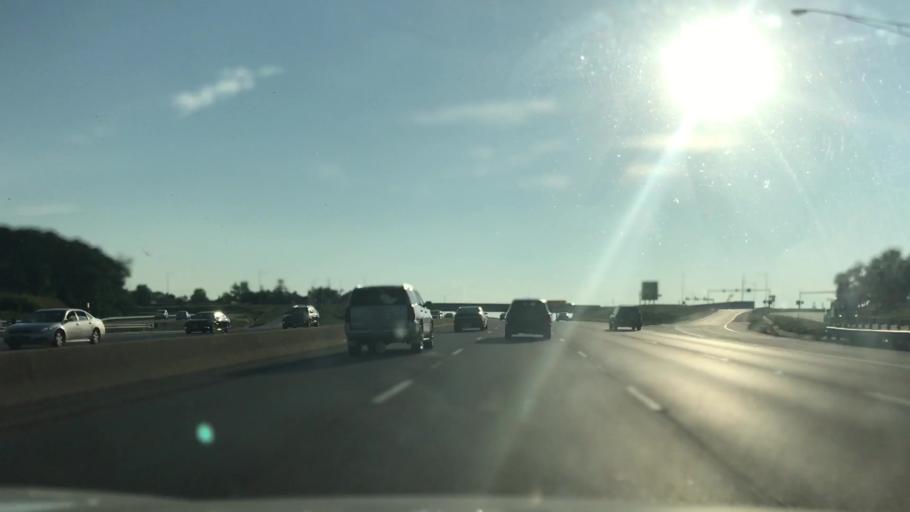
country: US
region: Missouri
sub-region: Saint Louis County
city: Town and Country
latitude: 38.6388
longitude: -90.4766
